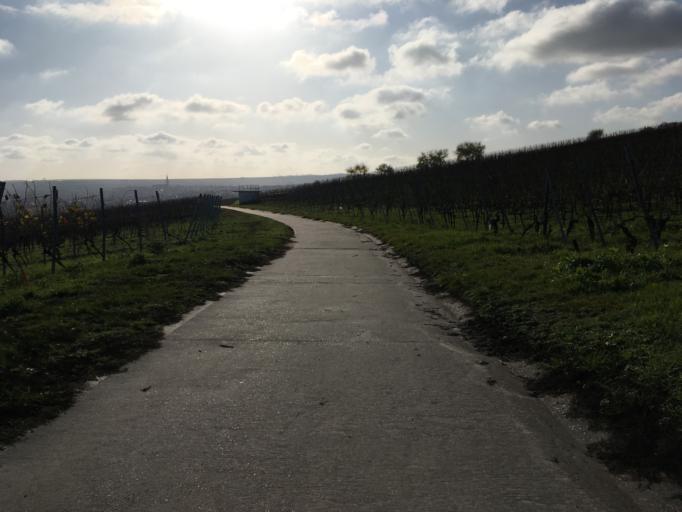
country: DE
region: Rheinland-Pfalz
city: Bodenheim
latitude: 49.9440
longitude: 8.3020
